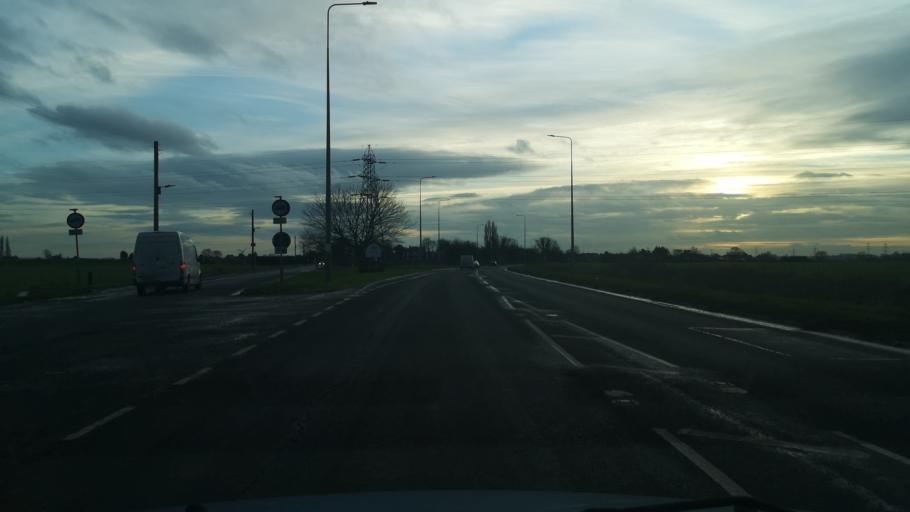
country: GB
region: England
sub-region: North Lincolnshire
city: Gunness
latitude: 53.5834
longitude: -0.7374
